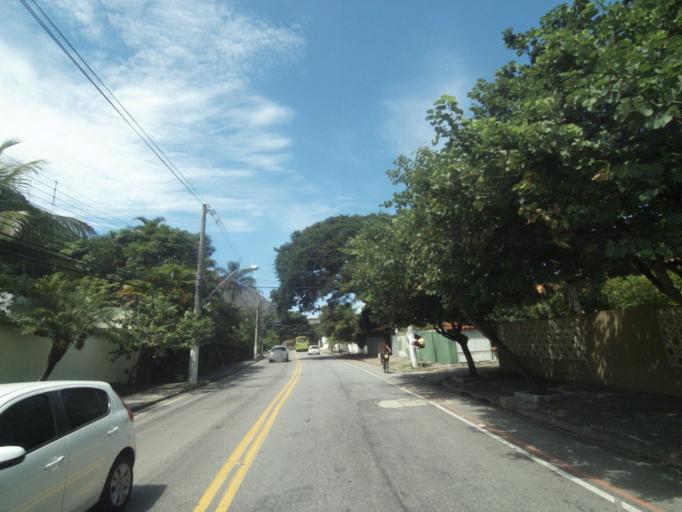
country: BR
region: Rio de Janeiro
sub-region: Niteroi
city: Niteroi
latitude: -22.9668
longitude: -43.0318
